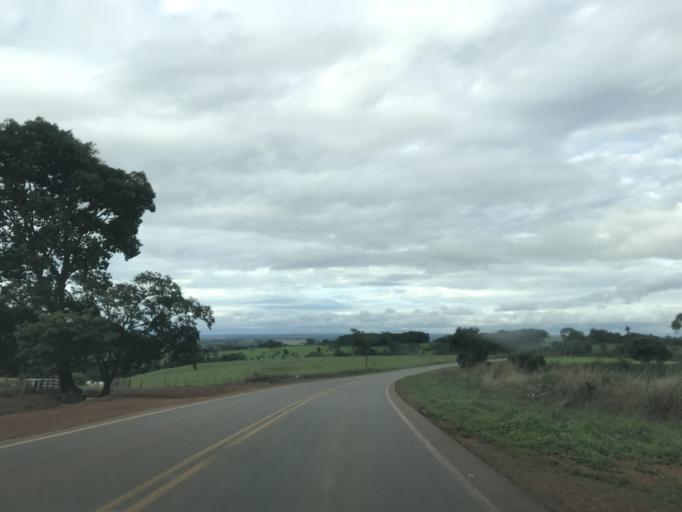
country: BR
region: Goias
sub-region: Vianopolis
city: Vianopolis
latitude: -16.7150
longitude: -48.4042
